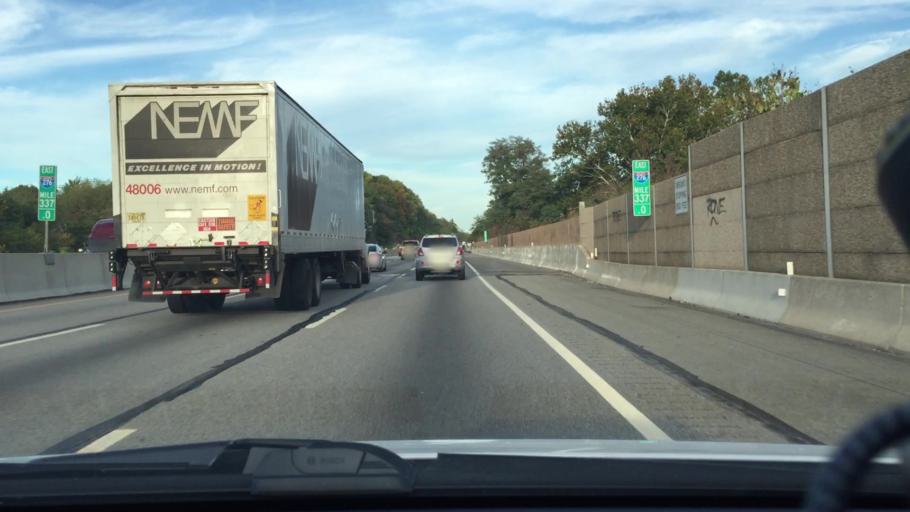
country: US
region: Pennsylvania
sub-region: Montgomery County
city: Fort Washington
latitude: 40.1272
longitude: -75.2197
